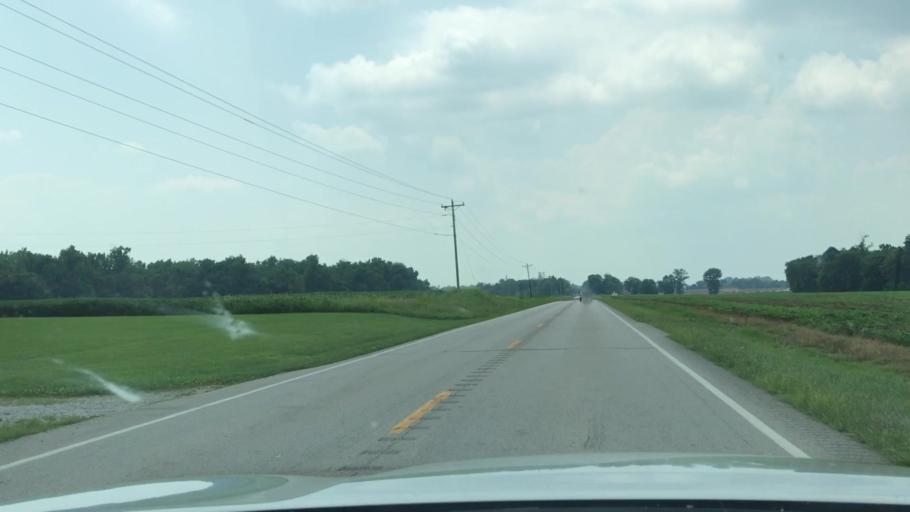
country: US
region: Kentucky
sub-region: Todd County
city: Guthrie
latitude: 36.6671
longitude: -87.1641
